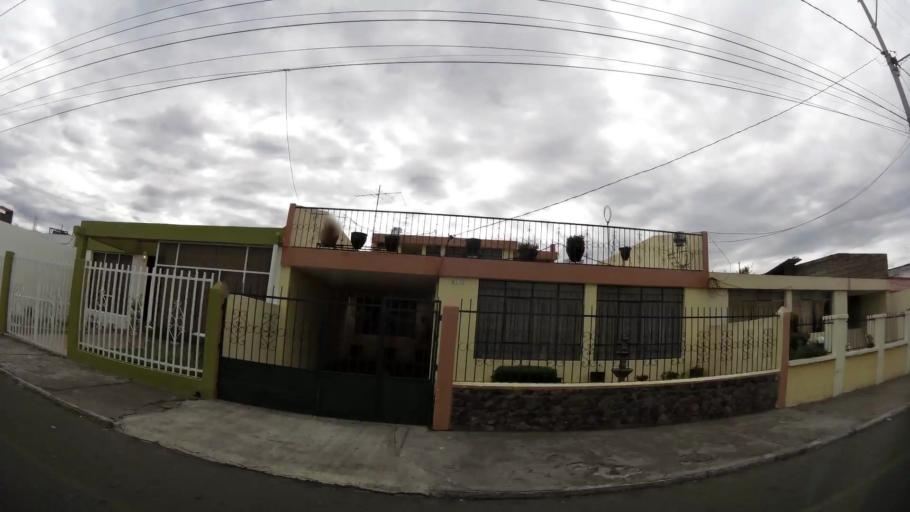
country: EC
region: Cotopaxi
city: Latacunga
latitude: -0.9432
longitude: -78.6158
